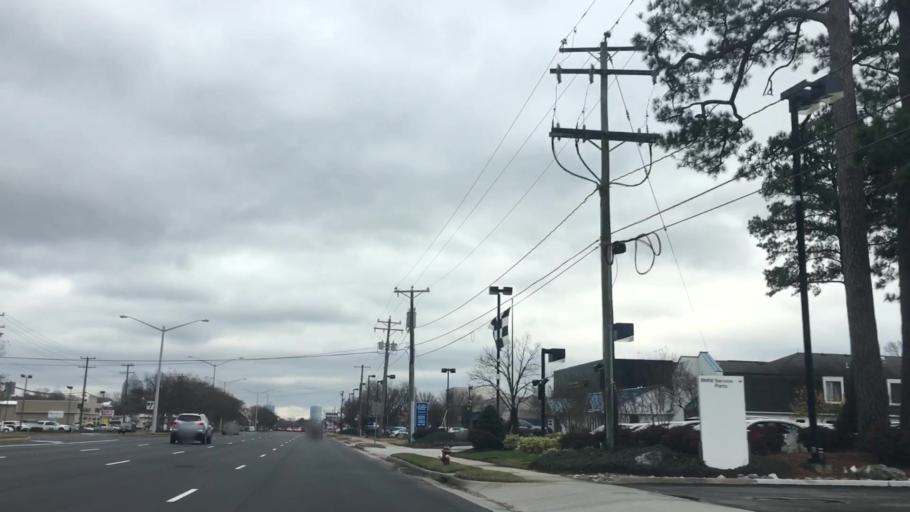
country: US
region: Virginia
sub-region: City of Chesapeake
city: Chesapeake
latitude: 36.8477
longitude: -76.1618
